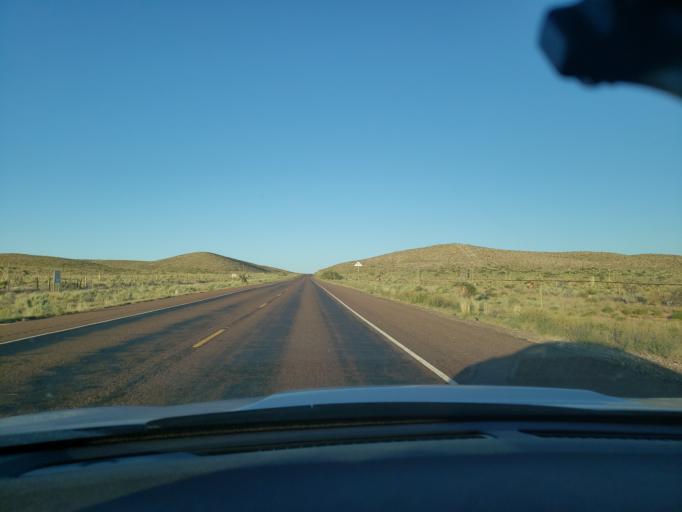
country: US
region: Texas
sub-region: El Paso County
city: Homestead Meadows South
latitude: 31.8267
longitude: -105.9011
